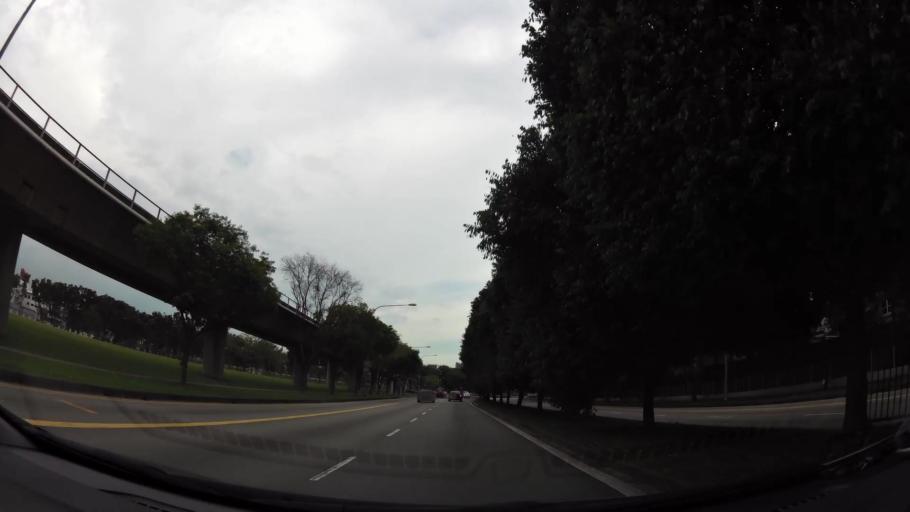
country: MY
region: Johor
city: Kampung Pasir Gudang Baru
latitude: 1.3852
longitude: 103.8427
